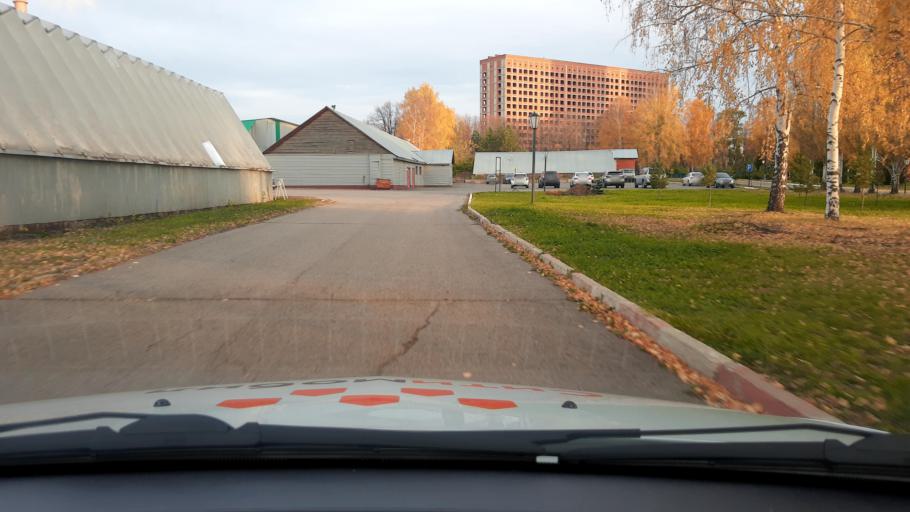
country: RU
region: Bashkortostan
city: Ufa
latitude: 54.7113
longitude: 56.0120
